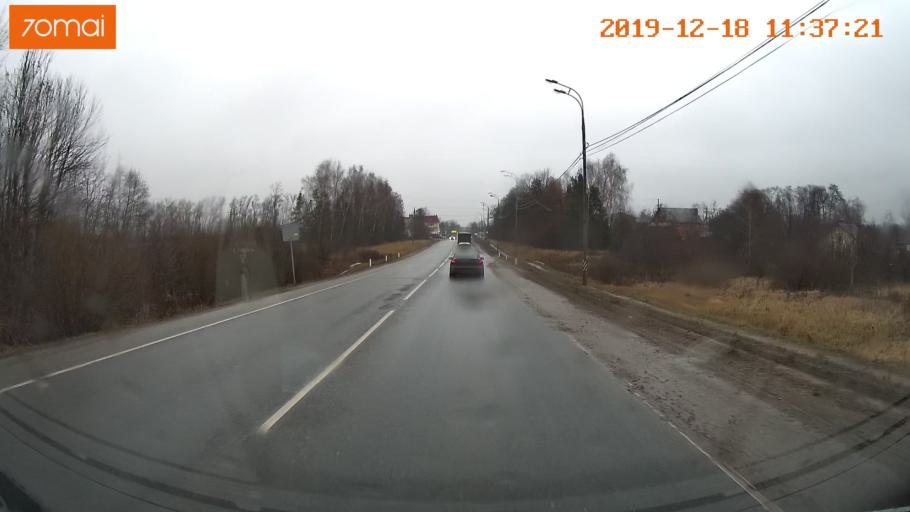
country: RU
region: Moskovskaya
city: Zvenigorod
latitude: 55.6896
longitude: 36.8961
